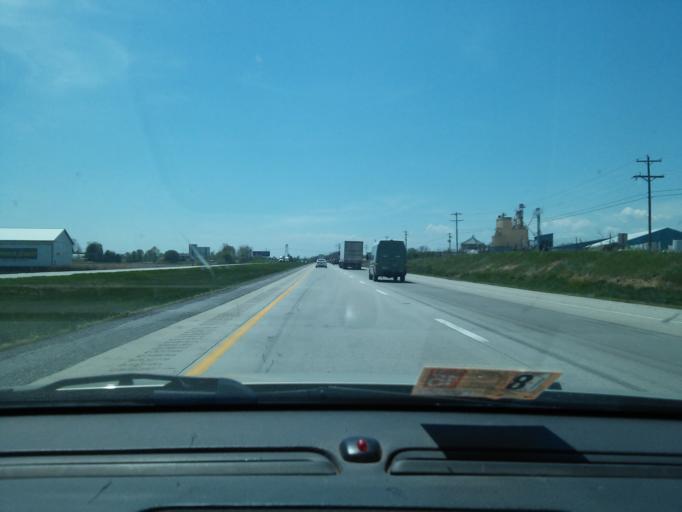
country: US
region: Pennsylvania
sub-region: Cumberland County
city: Shippensburg
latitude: 40.0120
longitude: -77.5387
